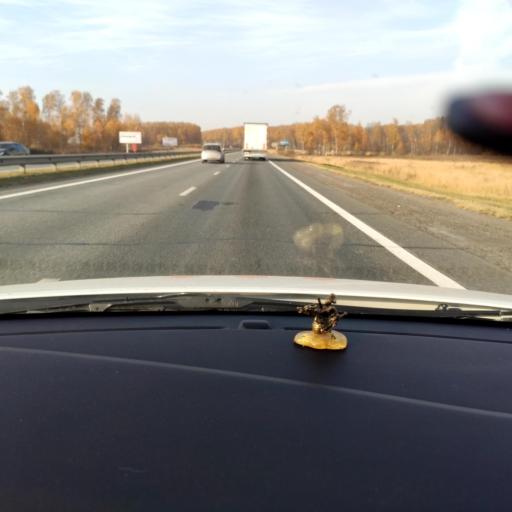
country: RU
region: Tatarstan
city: Osinovo
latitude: 55.9018
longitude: 48.9105
